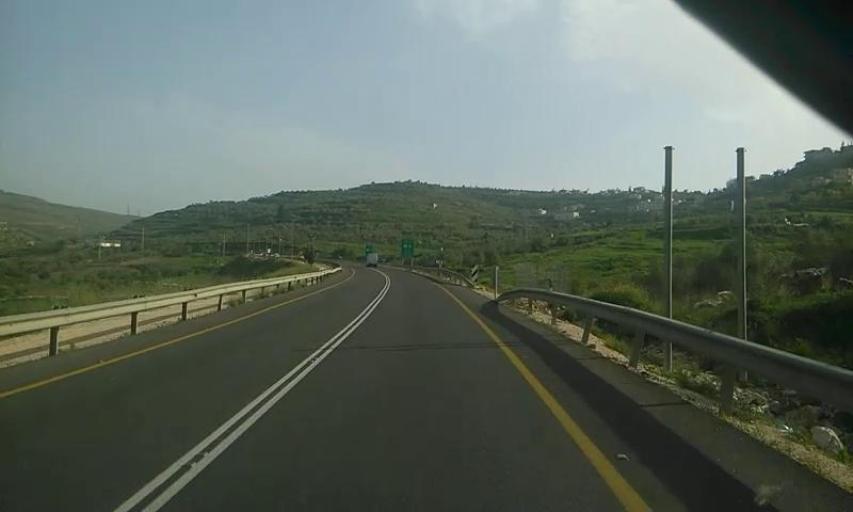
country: PS
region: West Bank
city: Jit
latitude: 32.2167
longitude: 35.1757
